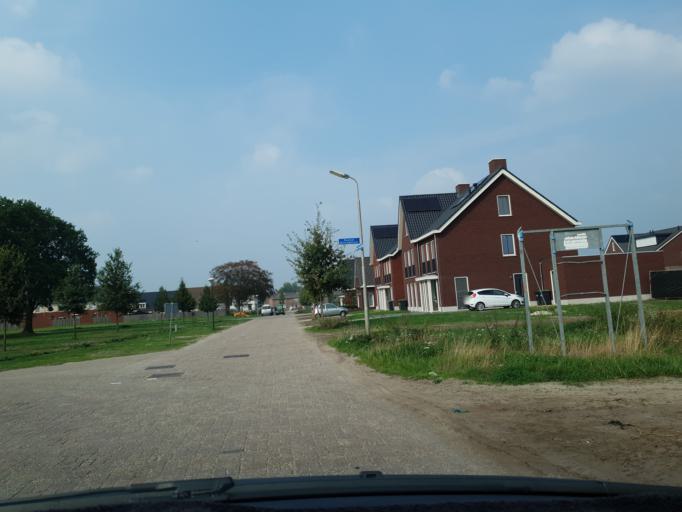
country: NL
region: North Brabant
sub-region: Gemeente Valkenswaard
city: Valkenswaard
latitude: 51.3440
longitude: 5.4326
